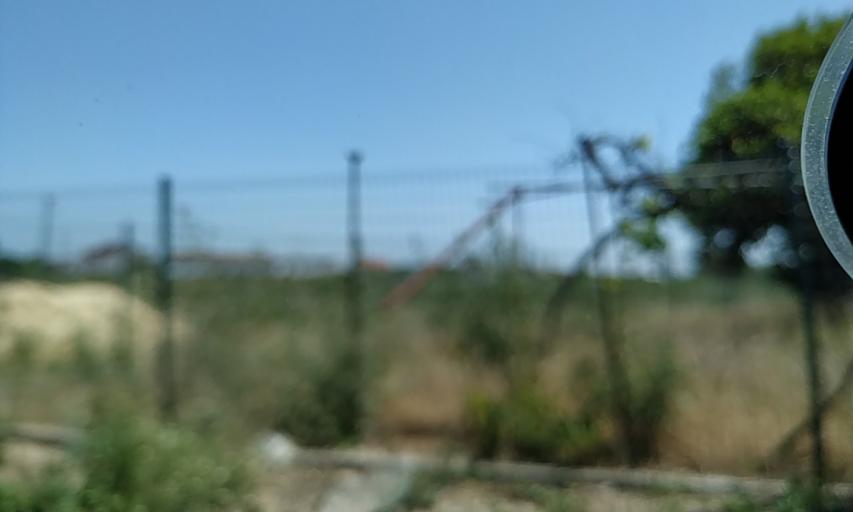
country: PT
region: Setubal
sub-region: Palmela
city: Palmela
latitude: 38.6153
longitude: -8.7584
